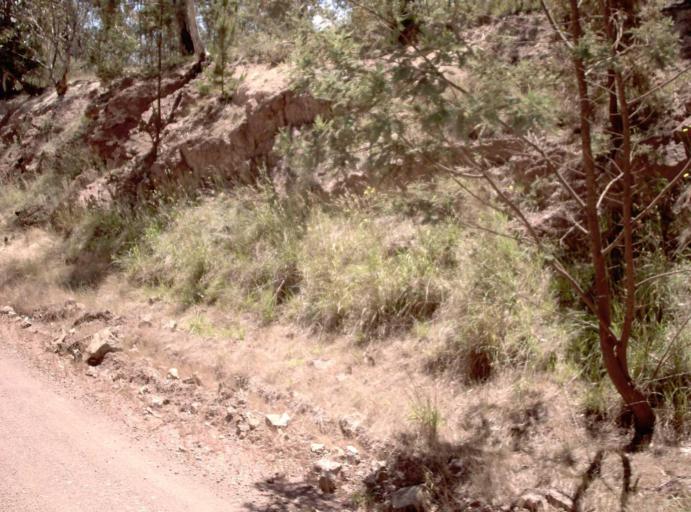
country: AU
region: New South Wales
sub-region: Snowy River
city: Jindabyne
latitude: -37.0311
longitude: 148.2733
